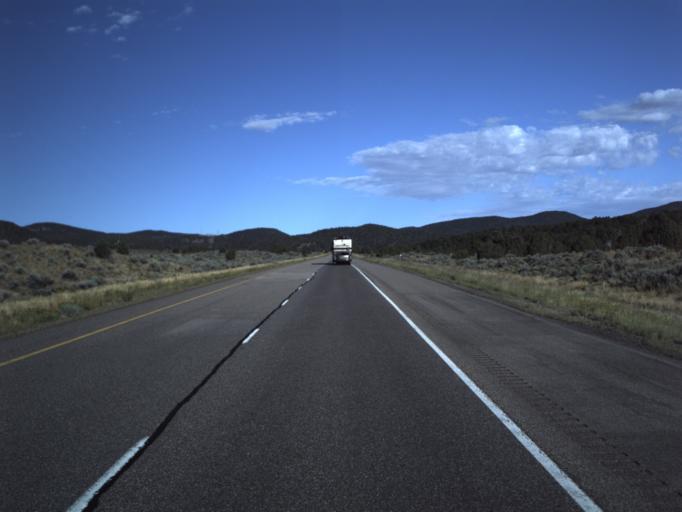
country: US
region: Utah
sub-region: Sevier County
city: Monroe
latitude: 38.5669
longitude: -112.4422
